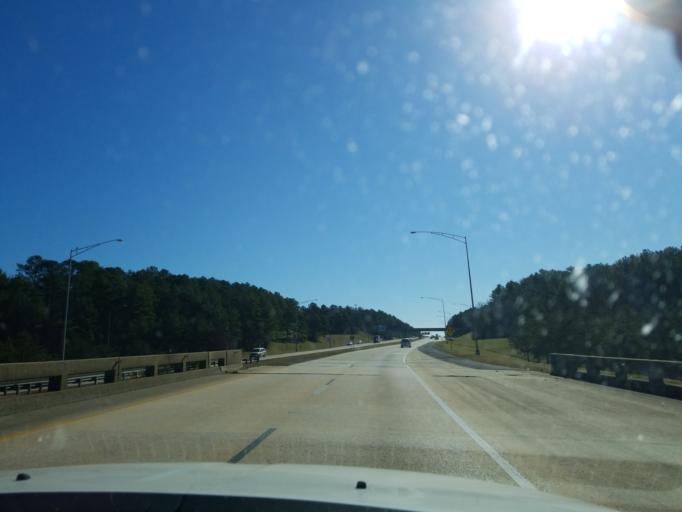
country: US
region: Alabama
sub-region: Jefferson County
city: Trussville
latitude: 33.5920
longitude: -86.6480
